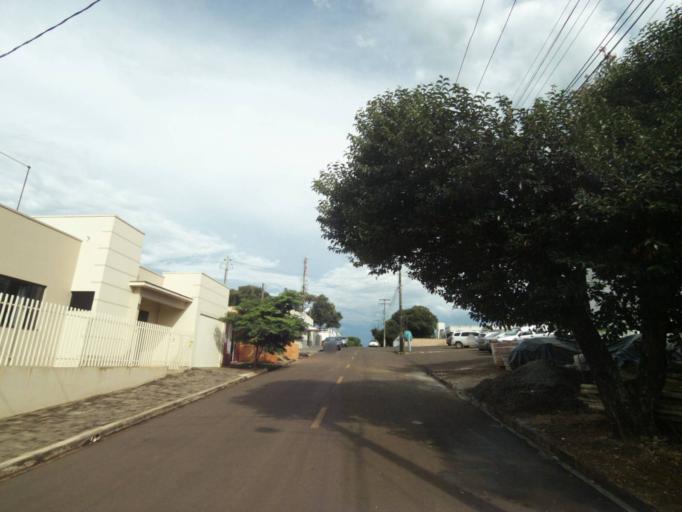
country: BR
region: Parana
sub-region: Guaraniacu
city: Guaraniacu
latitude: -25.1020
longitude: -52.8709
